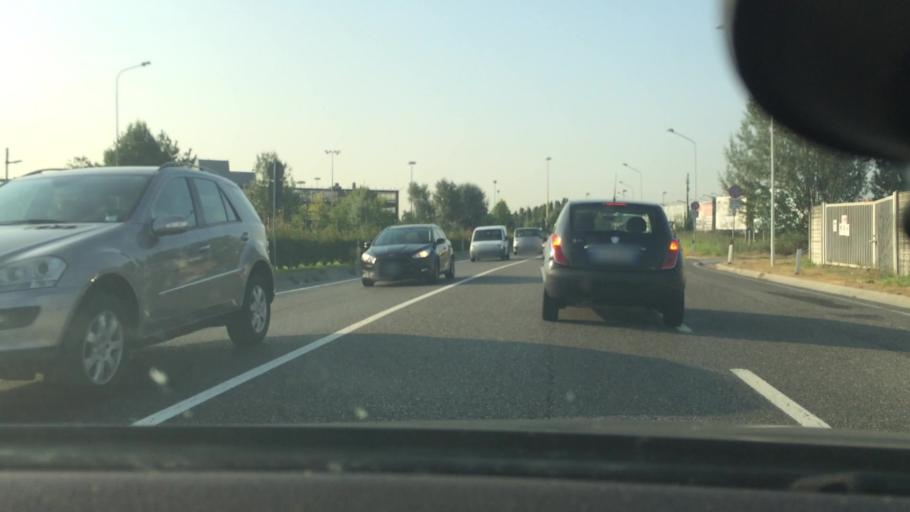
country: IT
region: Lombardy
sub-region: Citta metropolitana di Milano
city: Rho
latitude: 45.5227
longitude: 9.0690
